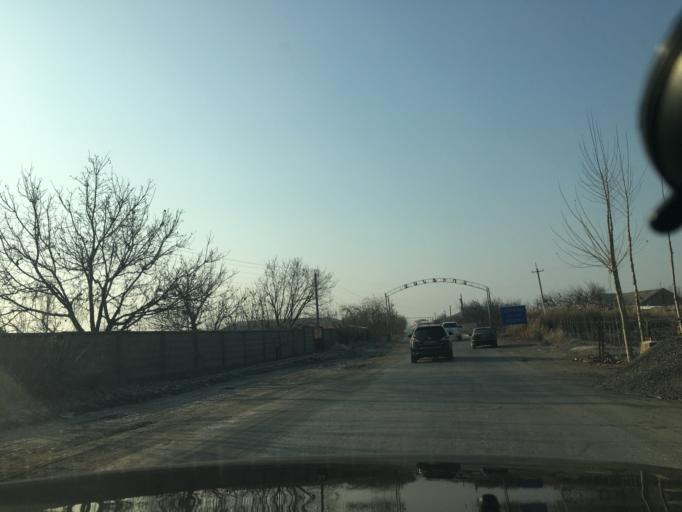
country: AM
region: Armavir
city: Janfida
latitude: 40.0522
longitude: 44.0335
